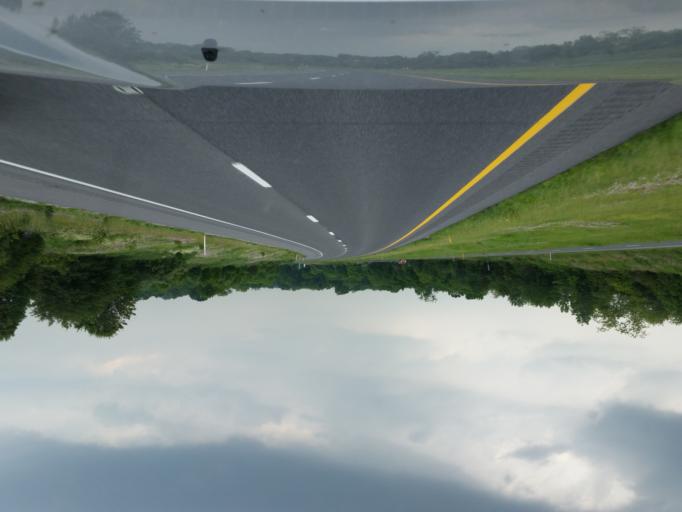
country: US
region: Pennsylvania
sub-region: Adams County
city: Biglerville
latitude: 39.9246
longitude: -77.1598
